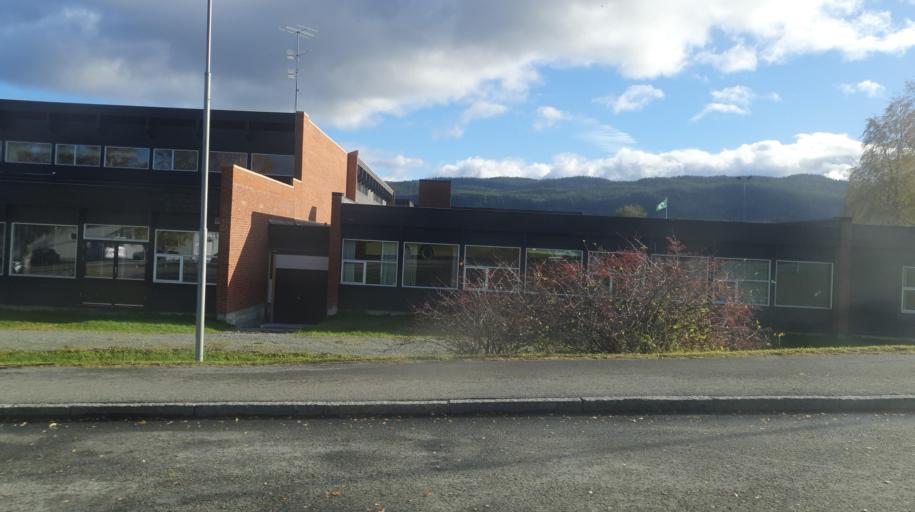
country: NO
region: Sor-Trondelag
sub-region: Klaebu
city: Klaebu
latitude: 63.3052
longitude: 10.4606
